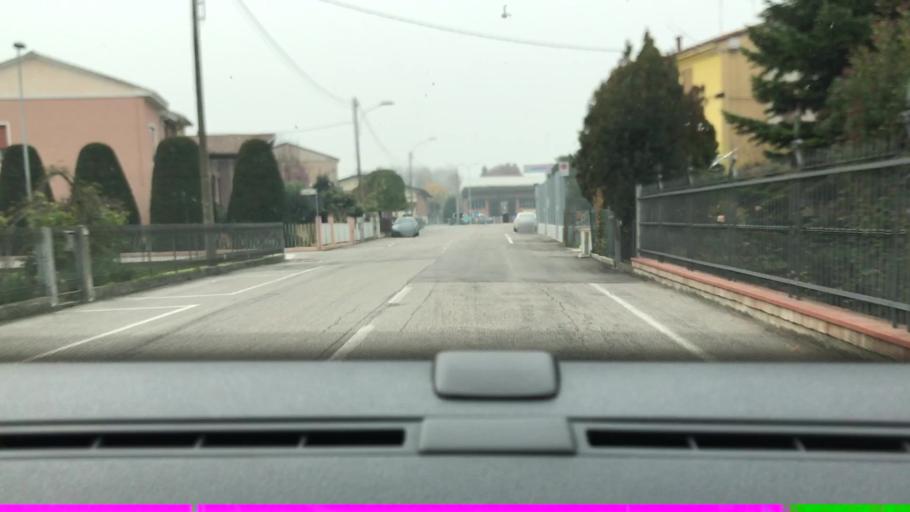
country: IT
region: Lombardy
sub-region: Provincia di Mantova
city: San Giacomo delle Segnate
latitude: 44.9727
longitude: 11.0312
